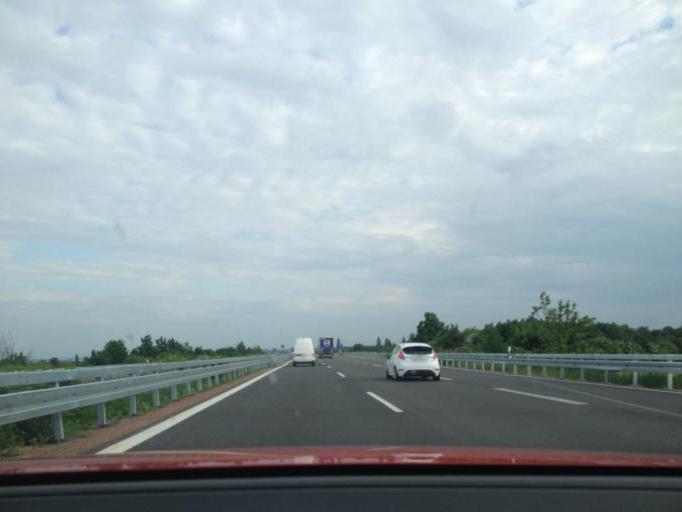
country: DE
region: Saxony-Anhalt
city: Oppin
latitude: 51.5446
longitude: 12.0113
